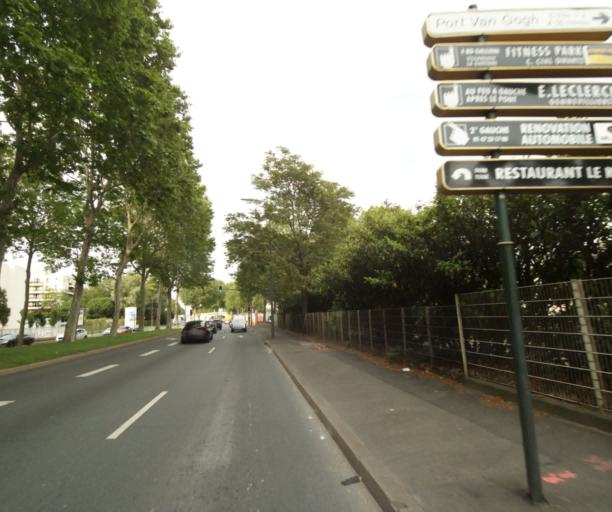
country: FR
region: Ile-de-France
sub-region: Departement des Hauts-de-Seine
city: Clichy
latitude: 48.9129
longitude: 2.3059
